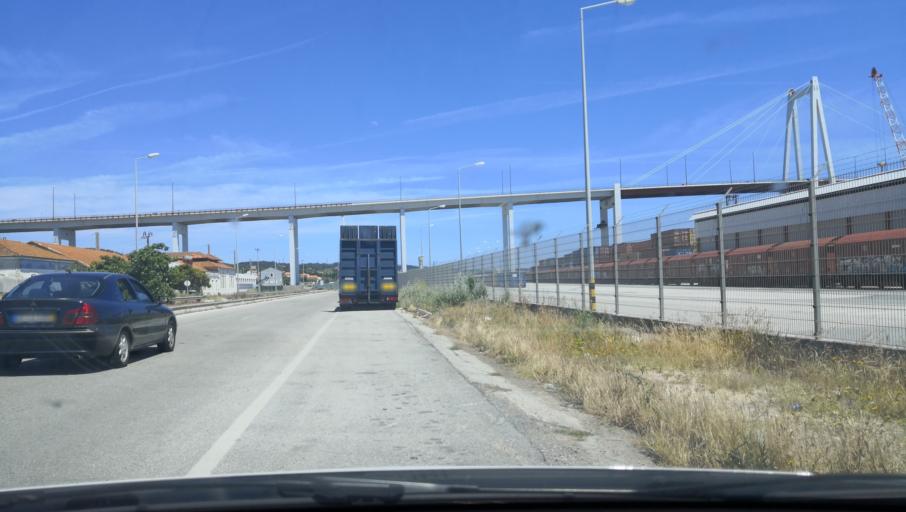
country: PT
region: Coimbra
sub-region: Figueira da Foz
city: Figueira da Foz
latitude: 40.1479
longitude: -8.8454
